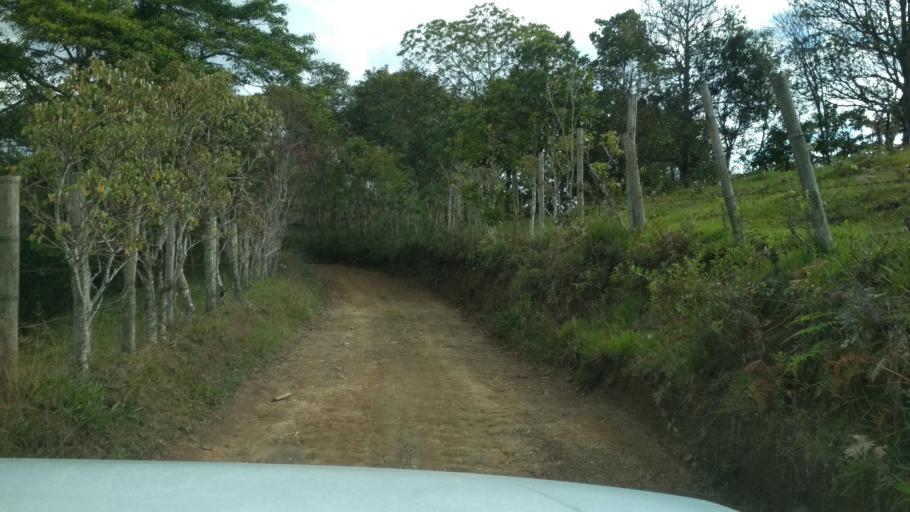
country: CO
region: Cauca
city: Lopez
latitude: 2.4028
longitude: -76.7135
